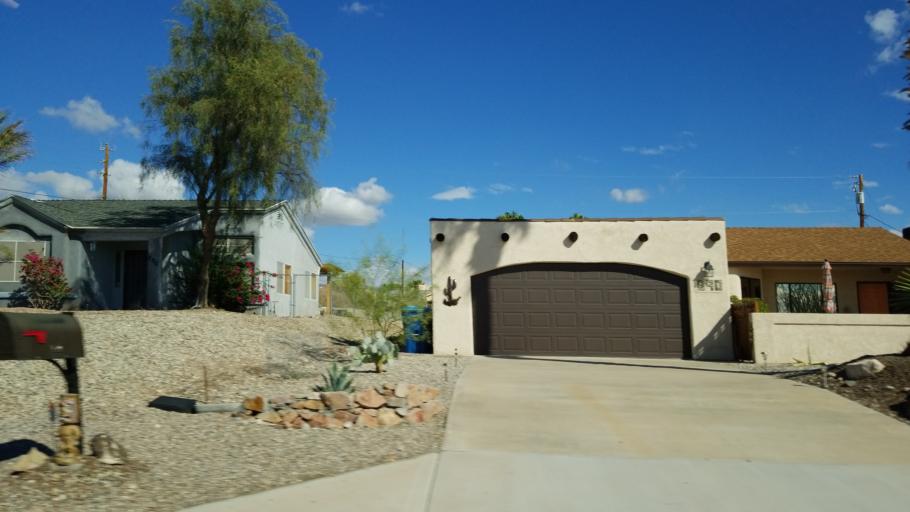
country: US
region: Arizona
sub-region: Mohave County
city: Lake Havasu City
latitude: 34.4790
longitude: -114.2672
